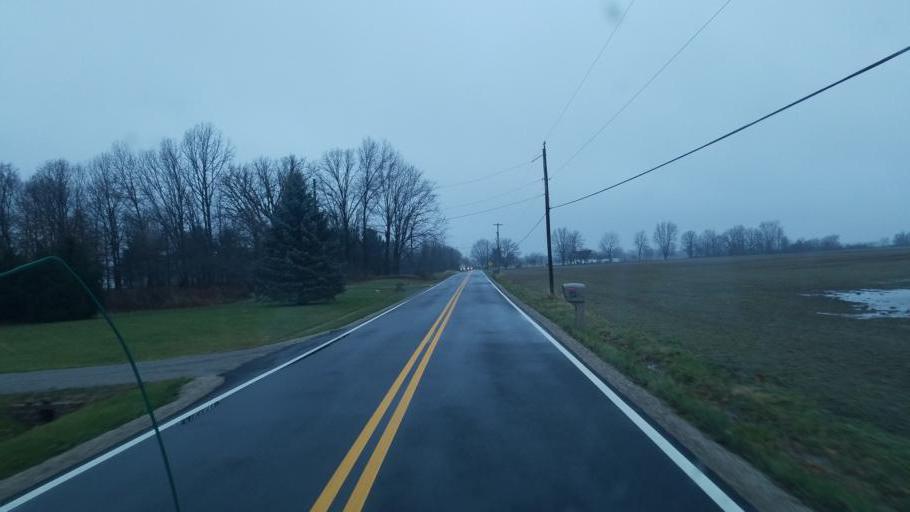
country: US
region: Ohio
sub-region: Delaware County
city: Delaware
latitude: 40.2698
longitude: -83.0023
